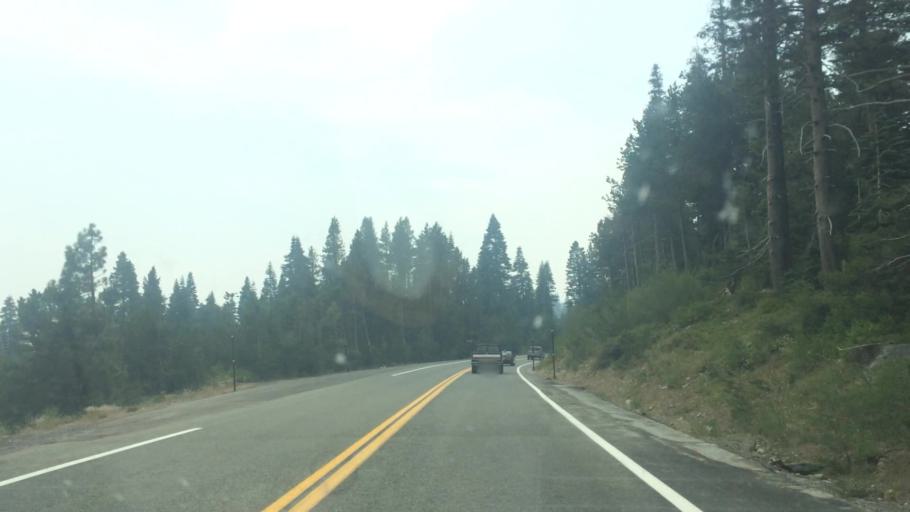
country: US
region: California
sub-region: Calaveras County
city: Arnold
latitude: 38.6127
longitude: -120.2215
